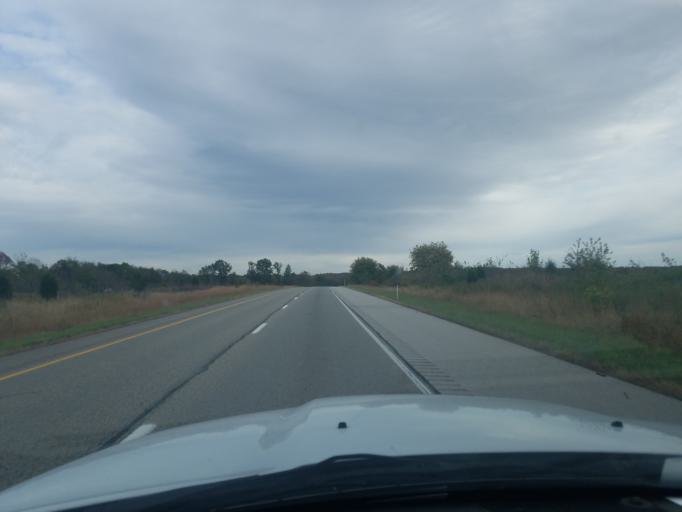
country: US
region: Indiana
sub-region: Spencer County
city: Dale
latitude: 38.1983
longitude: -87.1576
